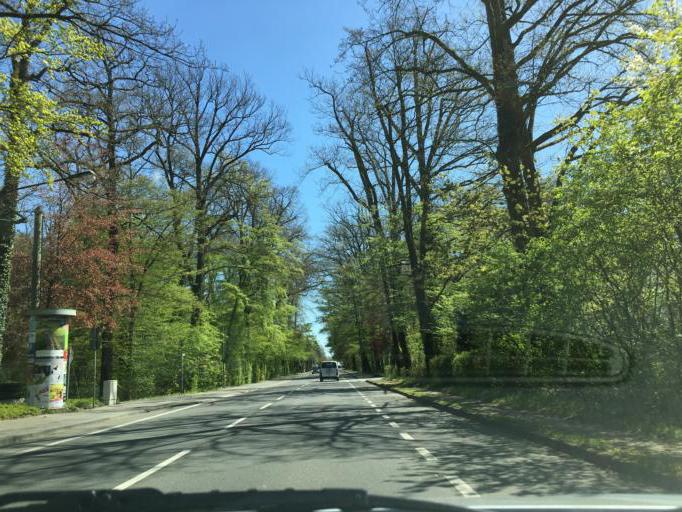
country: DE
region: Hesse
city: Dreieich
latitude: 50.0199
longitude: 8.6687
